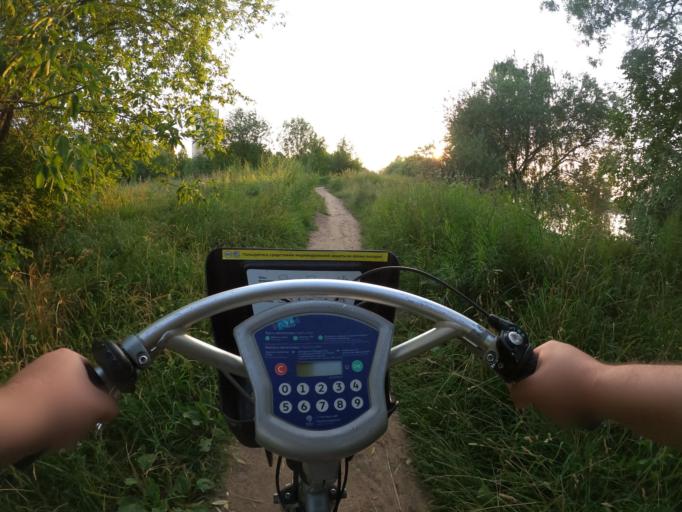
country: RU
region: Moscow
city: Shchukino
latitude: 55.8078
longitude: 37.4311
